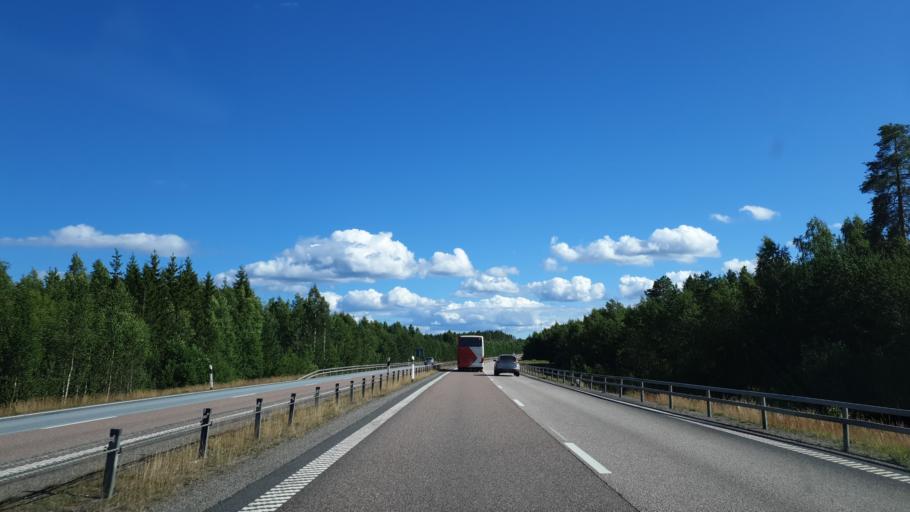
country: SE
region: Gaevleborg
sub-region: Hudiksvalls Kommun
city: Iggesund
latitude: 61.5168
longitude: 16.9809
